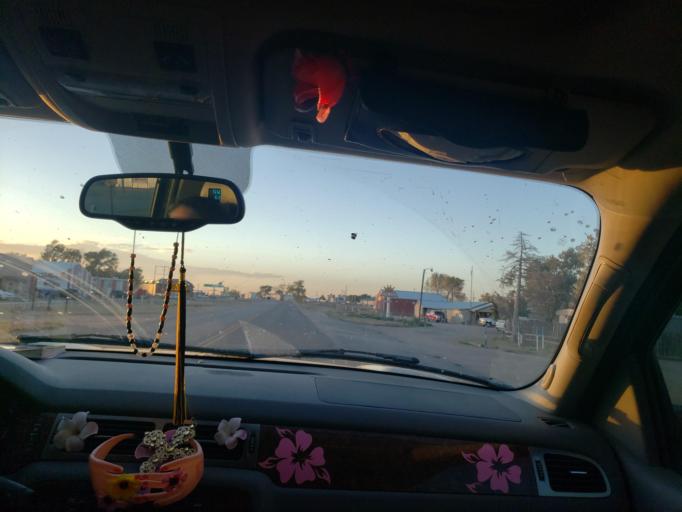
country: US
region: Kansas
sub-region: Finney County
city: Garden City
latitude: 37.9871
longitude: -100.9131
